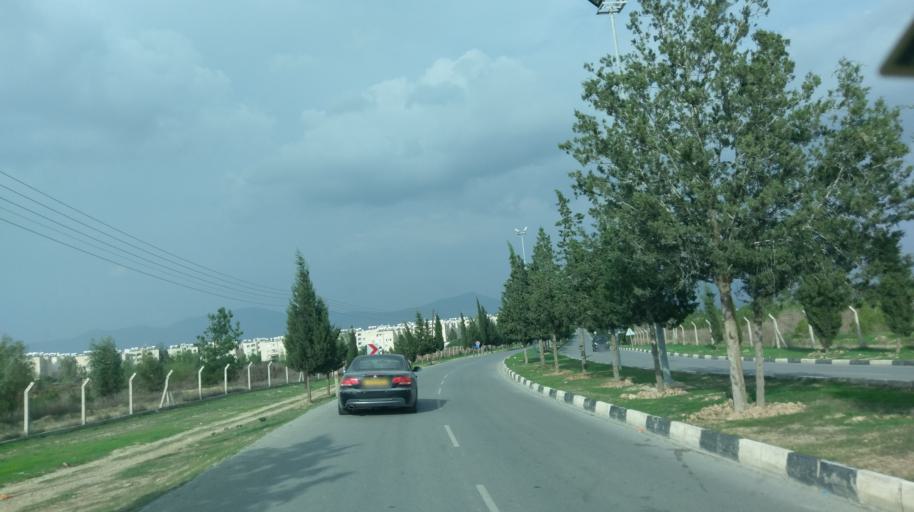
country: CY
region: Lefkosia
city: Nicosia
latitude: 35.1849
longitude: 33.3227
